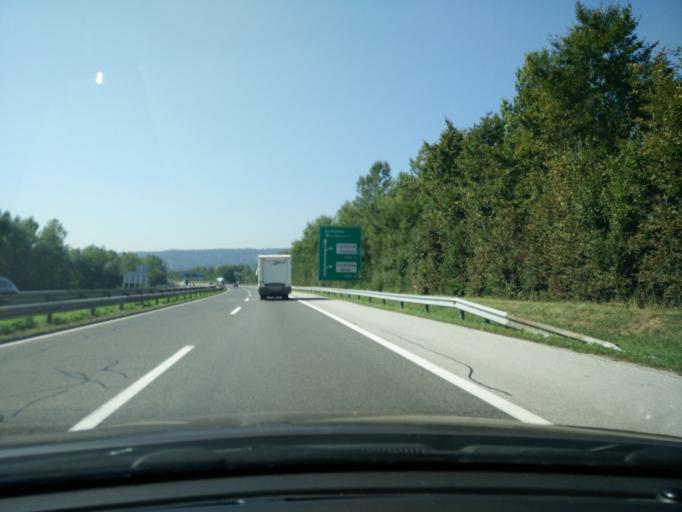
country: SI
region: Medvode
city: Zgornje Pirnice
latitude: 46.1178
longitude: 14.4763
